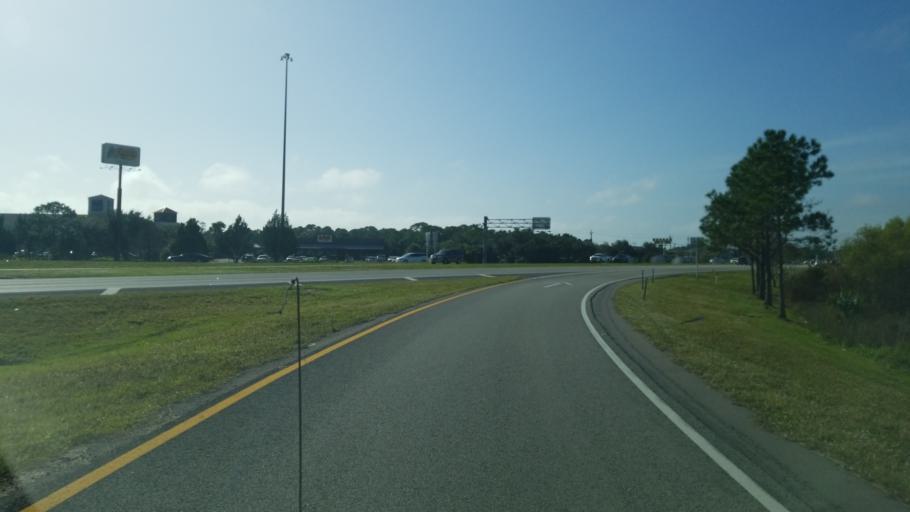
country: US
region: Florida
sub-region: Charlotte County
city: Harbour Heights
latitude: 27.0198
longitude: -82.0495
